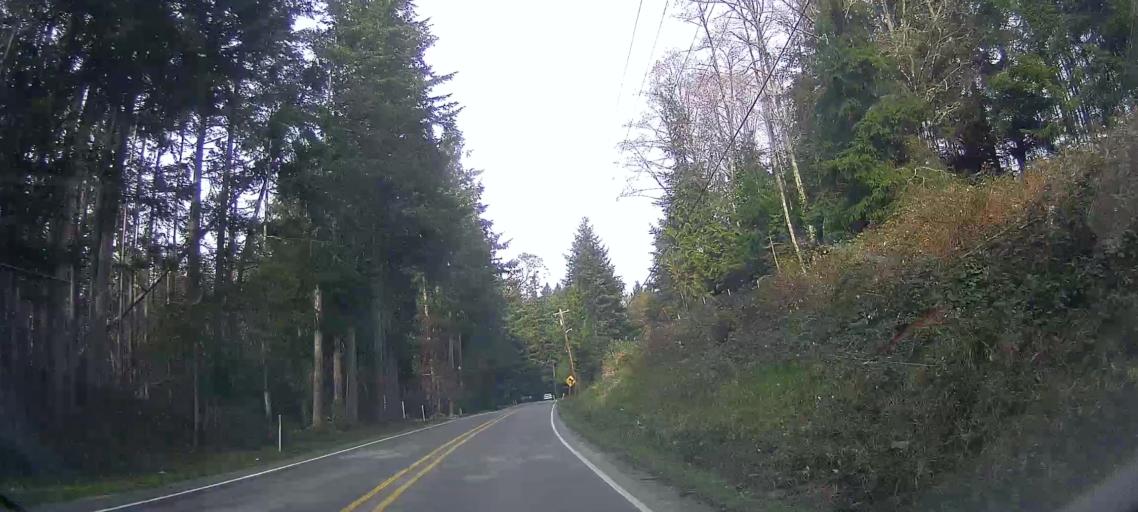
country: US
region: Washington
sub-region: Island County
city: Langley
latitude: 48.1190
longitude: -122.4509
